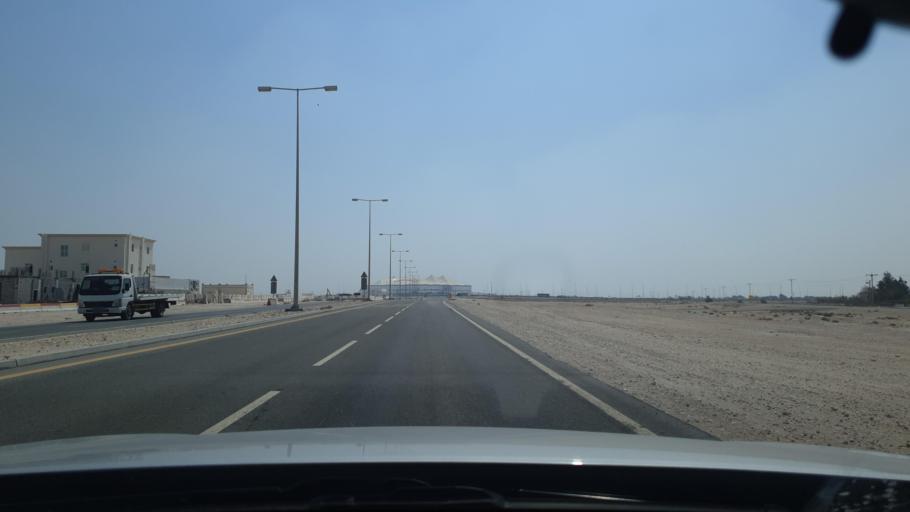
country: QA
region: Al Khawr
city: Al Khawr
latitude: 25.6709
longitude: 51.4715
